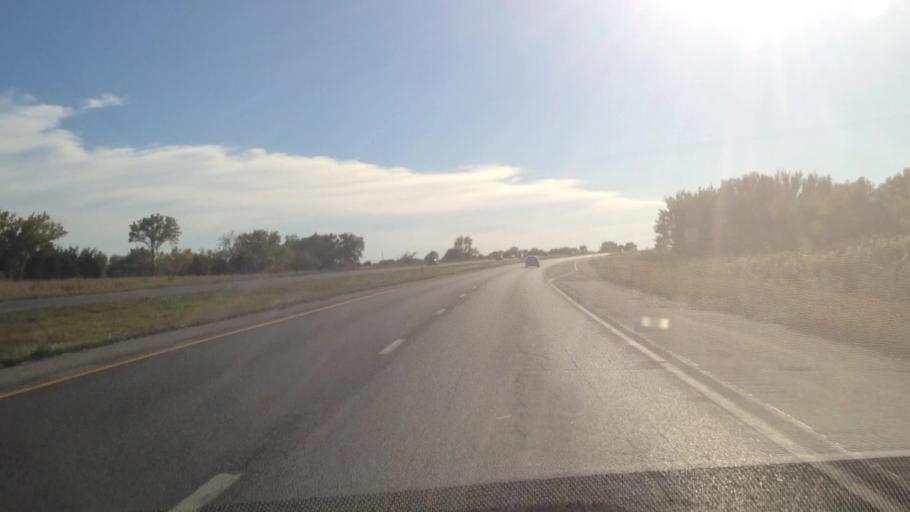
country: US
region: Kansas
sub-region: Douglas County
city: Eudora
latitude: 38.9484
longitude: -95.0320
